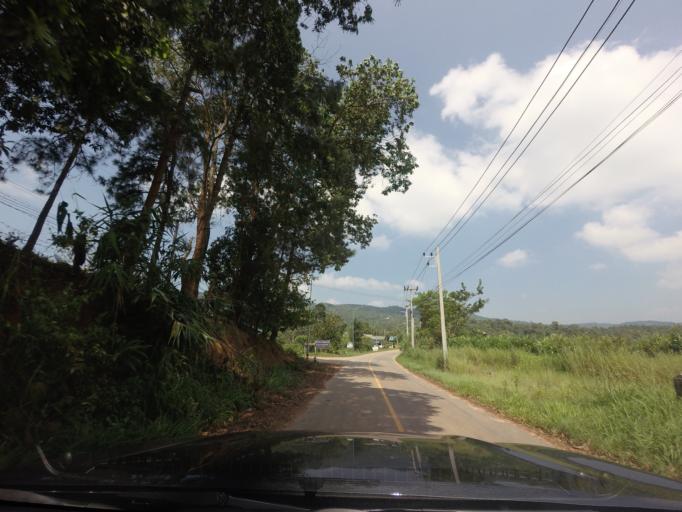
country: TH
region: Loei
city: Na Haeo
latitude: 17.4706
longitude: 100.9208
